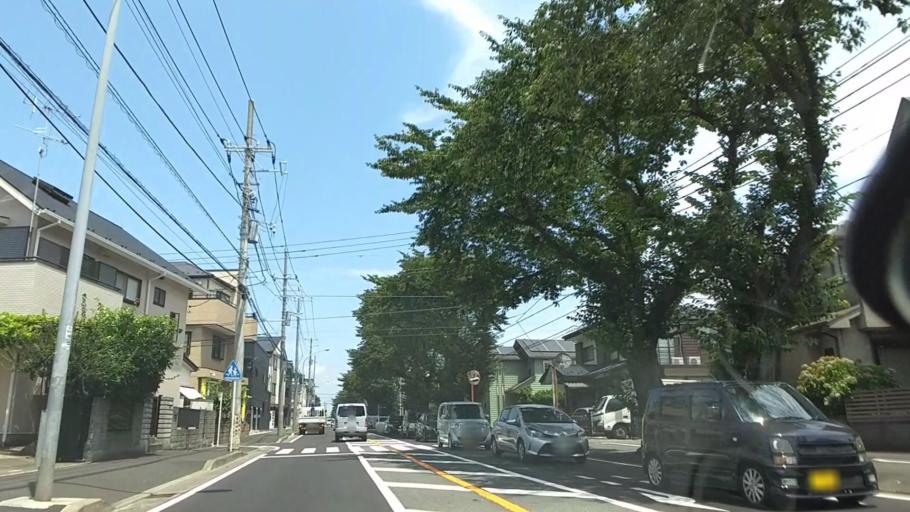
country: JP
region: Kanagawa
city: Minami-rinkan
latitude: 35.4732
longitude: 139.4807
